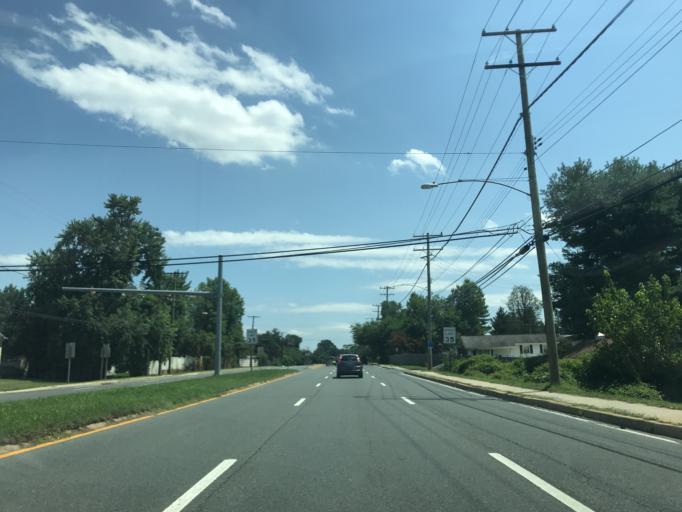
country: US
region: Maryland
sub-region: Montgomery County
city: Wheaton
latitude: 39.0393
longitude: -77.0423
